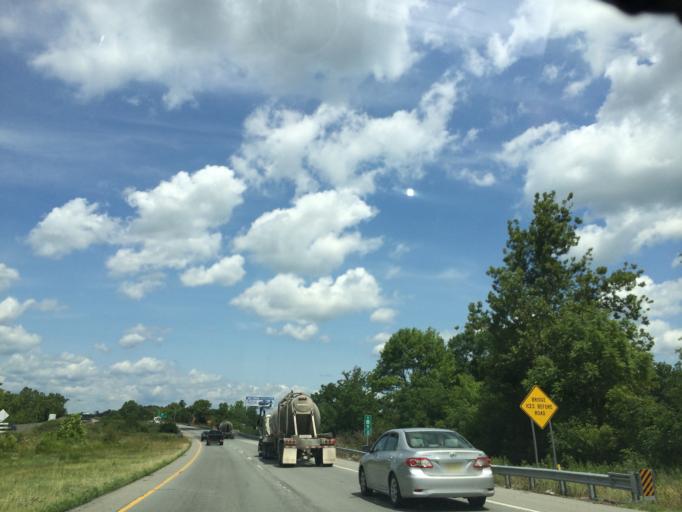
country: US
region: Pennsylvania
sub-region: Northampton County
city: Tatamy
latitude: 40.7473
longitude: -75.2642
